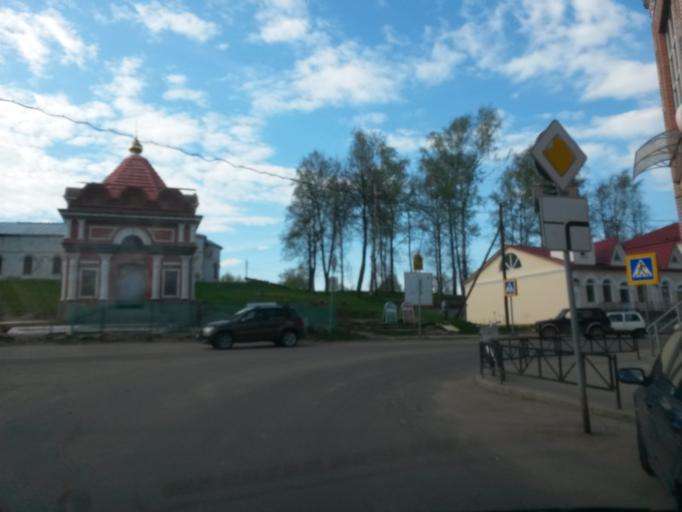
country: RU
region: Jaroslavl
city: Myshkin
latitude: 57.7838
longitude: 38.4520
